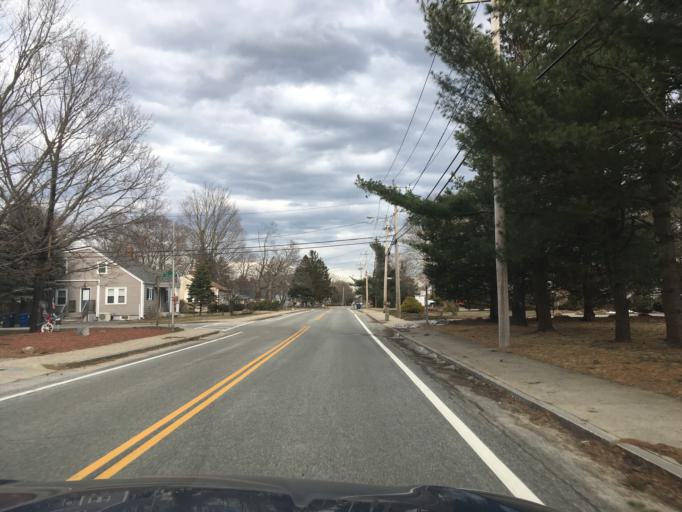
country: US
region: Rhode Island
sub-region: Kent County
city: East Greenwich
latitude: 41.6608
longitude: -71.4202
